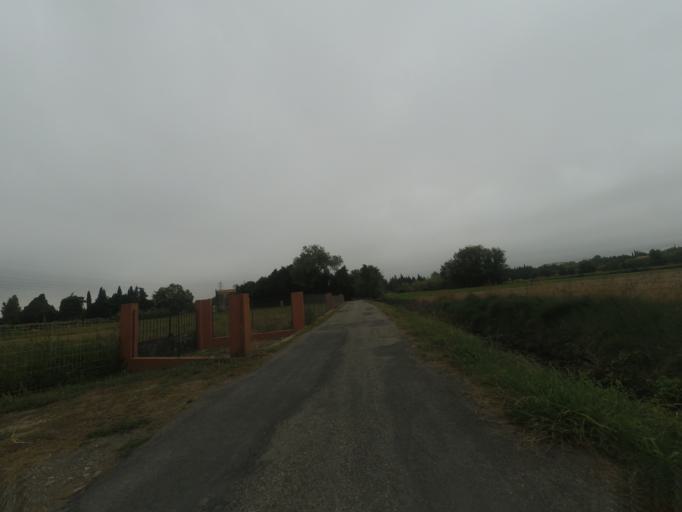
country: FR
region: Languedoc-Roussillon
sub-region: Departement des Pyrenees-Orientales
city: Saint-Esteve
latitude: 42.7010
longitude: 2.8381
